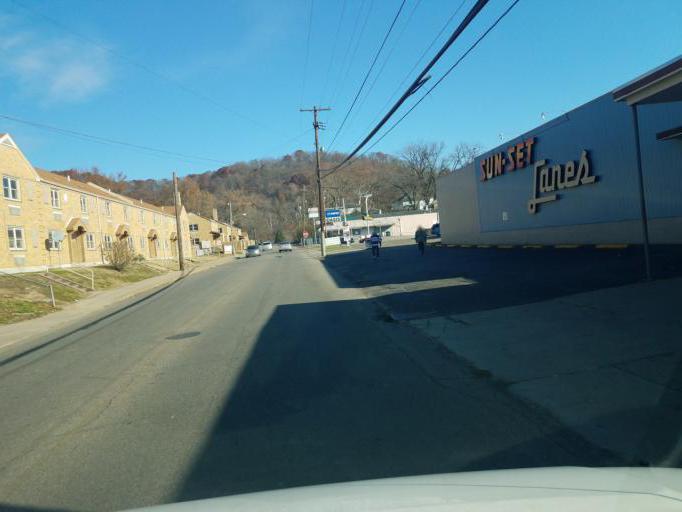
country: US
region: Kentucky
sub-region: Greenup County
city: South Shore
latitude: 38.7441
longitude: -82.9704
